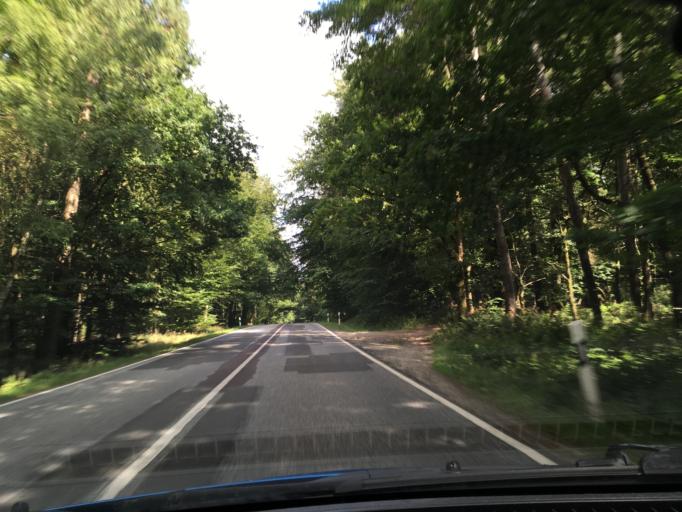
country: DE
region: Mecklenburg-Vorpommern
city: Lubtheen
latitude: 53.3993
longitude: 11.0310
